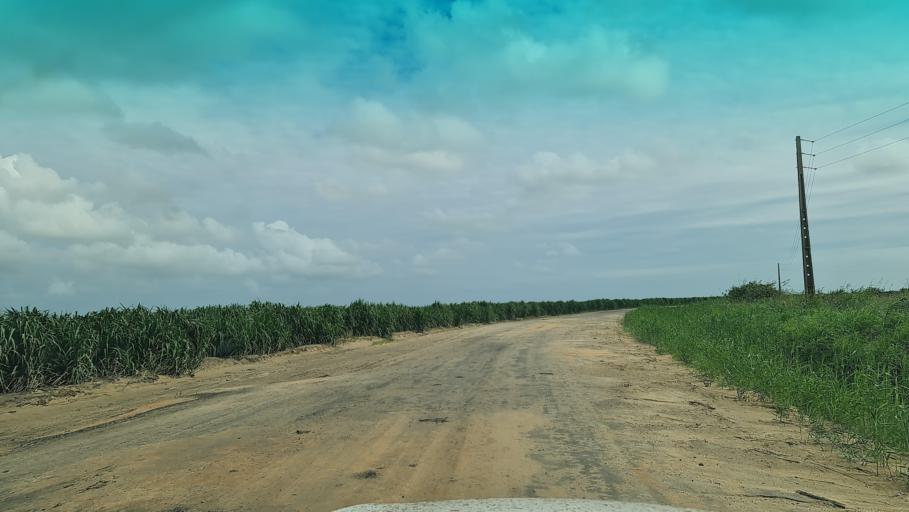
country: MZ
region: Maputo
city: Manhica
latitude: -25.4616
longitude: 32.8187
